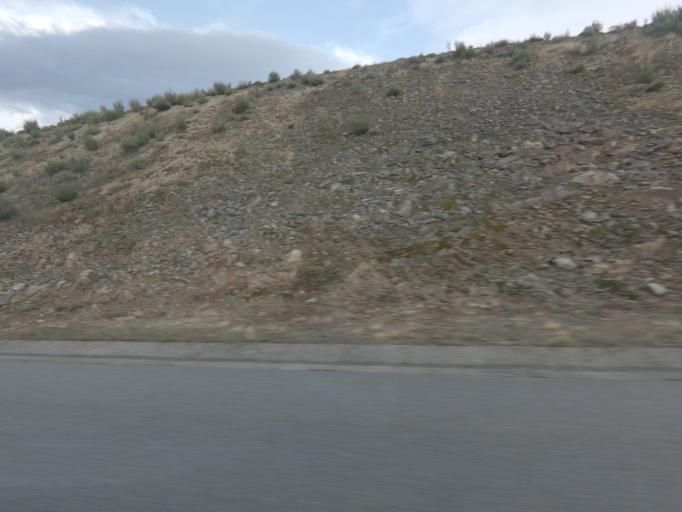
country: PT
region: Viseu
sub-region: Tarouca
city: Tarouca
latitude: 40.9907
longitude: -7.8827
